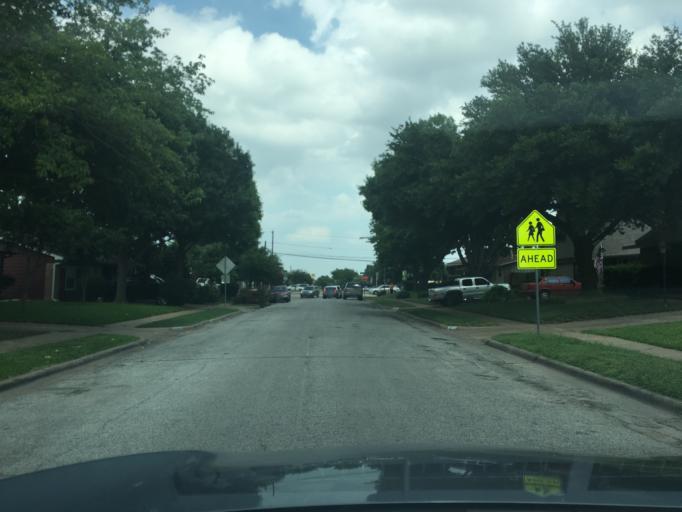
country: US
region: Texas
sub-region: Dallas County
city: Garland
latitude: 32.9141
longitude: -96.6840
